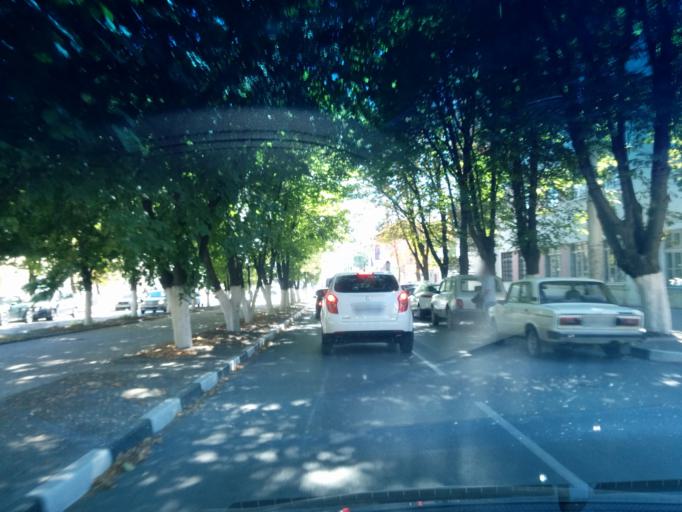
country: RU
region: Rostov
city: Shakhty
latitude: 47.7113
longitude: 40.2075
